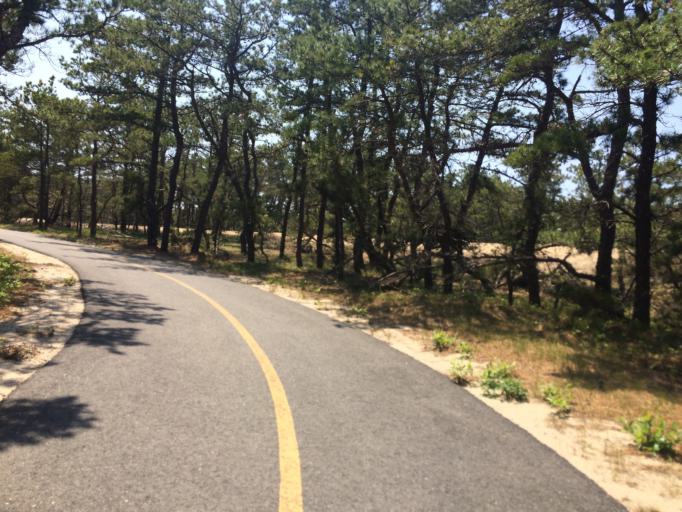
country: US
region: Massachusetts
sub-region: Barnstable County
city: Provincetown
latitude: 42.0654
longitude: -70.2152
